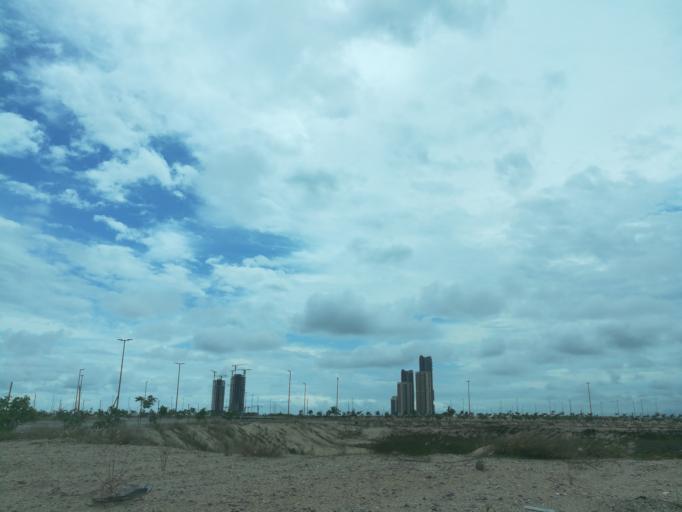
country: NG
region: Lagos
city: Ikoyi
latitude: 6.4109
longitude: 3.4210
